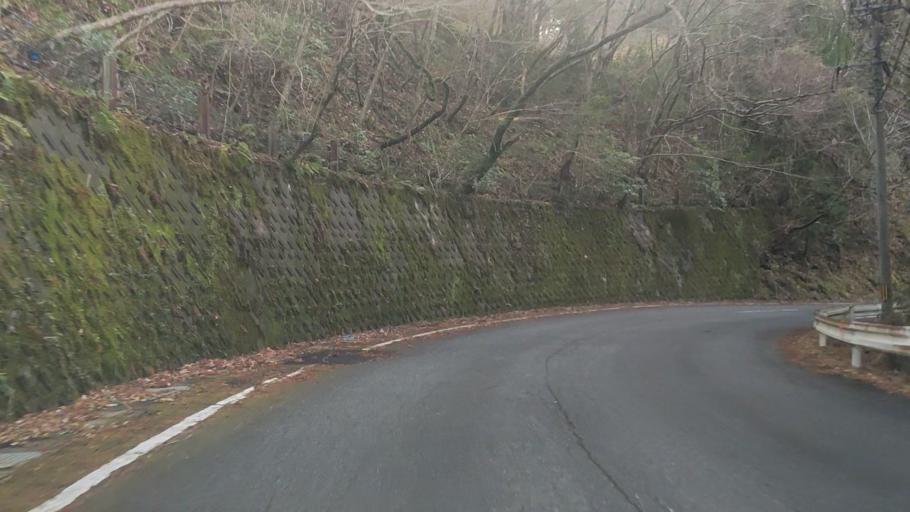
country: JP
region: Kumamoto
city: Matsubase
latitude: 32.4902
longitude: 130.9035
